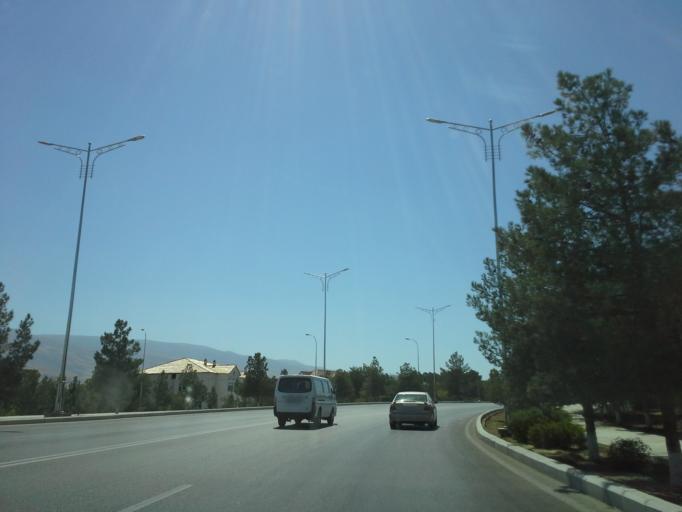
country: TM
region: Ahal
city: Ashgabat
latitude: 37.9293
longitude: 58.3149
